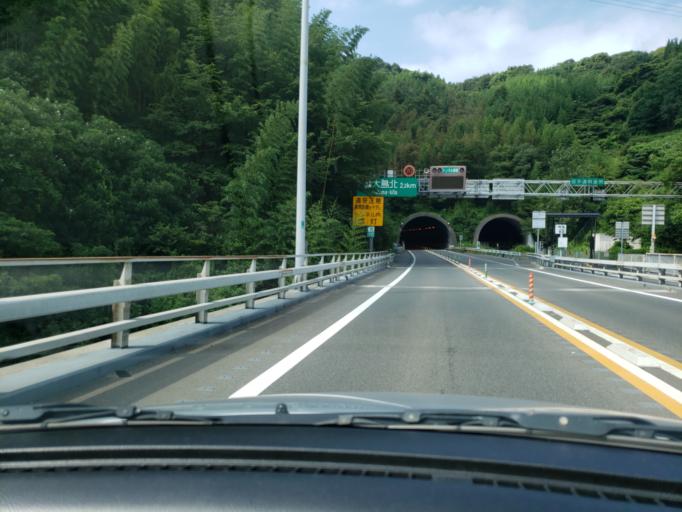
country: JP
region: Hiroshima
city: Innoshima
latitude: 34.1891
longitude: 133.0699
